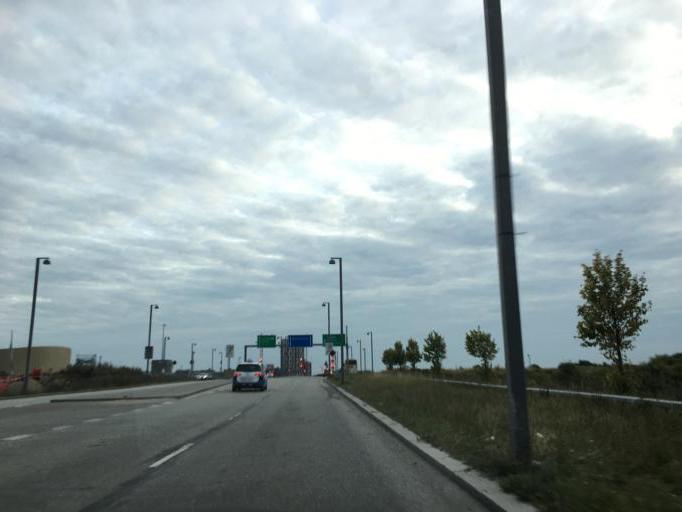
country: DK
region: Capital Region
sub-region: Tarnby Kommune
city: Tarnby
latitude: 55.6303
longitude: 12.5715
